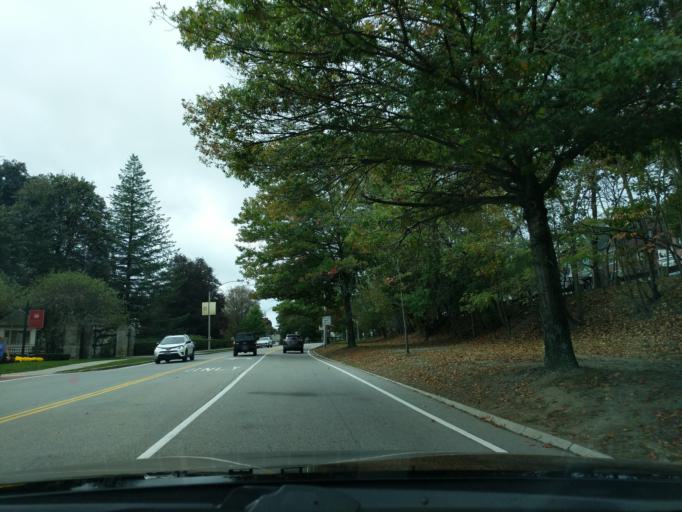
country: US
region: Massachusetts
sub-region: Middlesex County
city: Watertown
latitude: 42.3380
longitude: -71.1712
